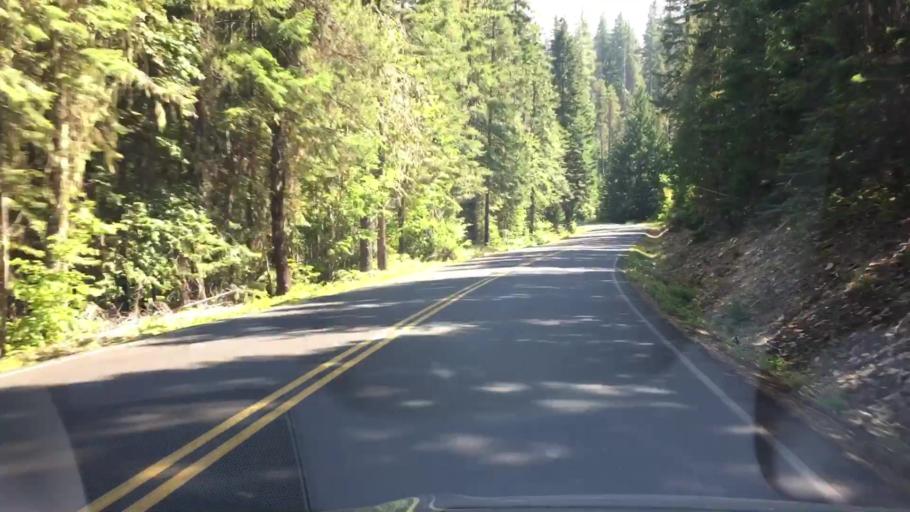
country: US
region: Washington
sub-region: Klickitat County
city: White Salmon
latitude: 46.0541
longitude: -121.5642
